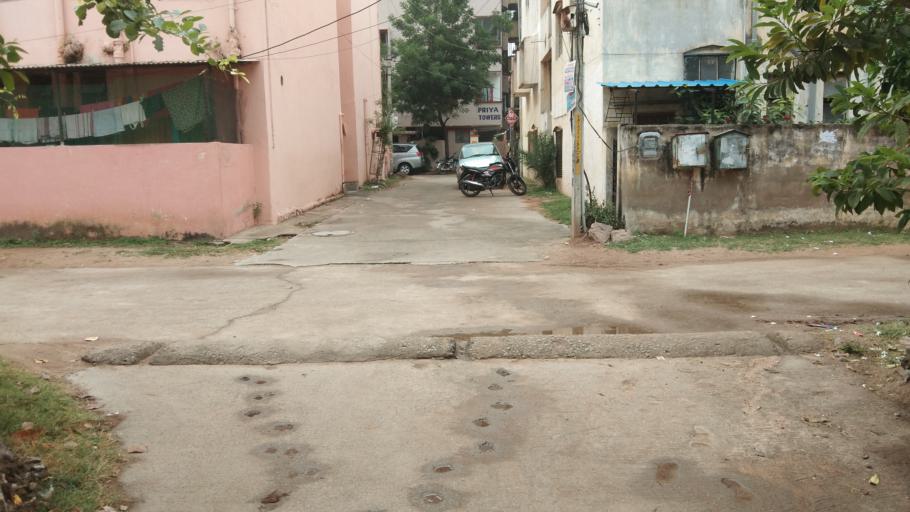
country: IN
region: Telangana
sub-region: Hyderabad
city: Malkajgiri
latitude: 17.4611
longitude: 78.5391
